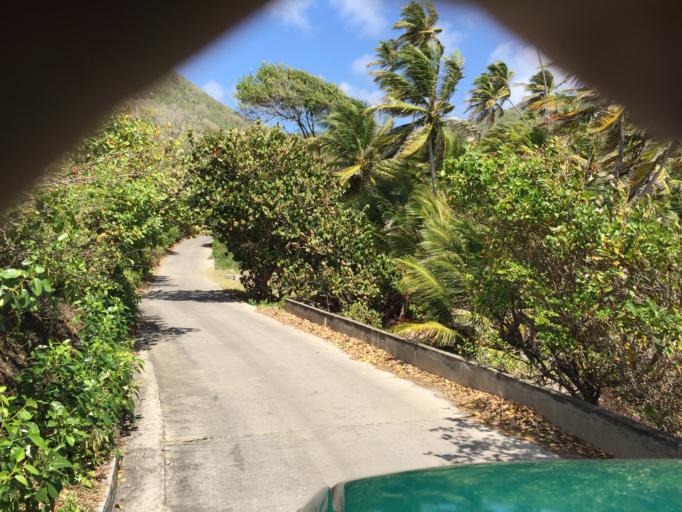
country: VC
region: Grenadines
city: Port Elizabeth
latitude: 13.0235
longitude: -61.2188
